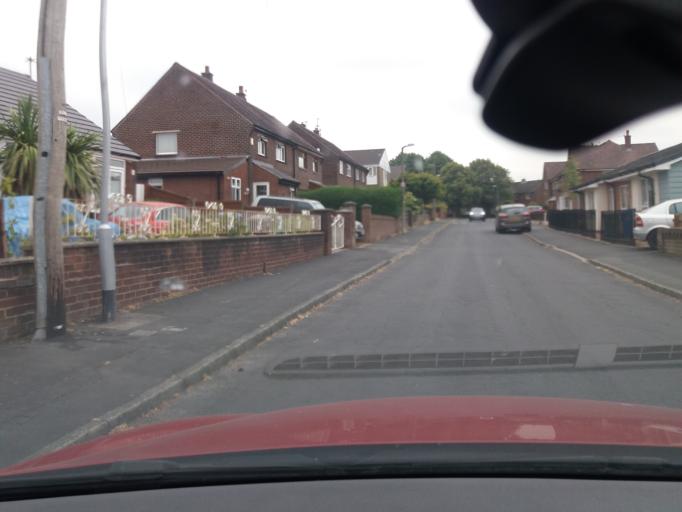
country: GB
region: England
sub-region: Lancashire
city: Chorley
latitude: 53.6453
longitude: -2.6418
